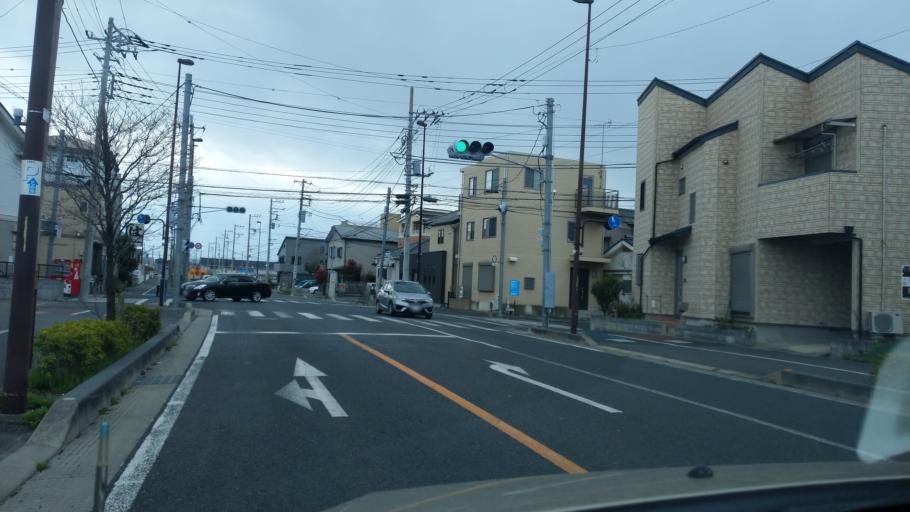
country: JP
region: Saitama
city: Yono
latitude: 35.8686
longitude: 139.6329
